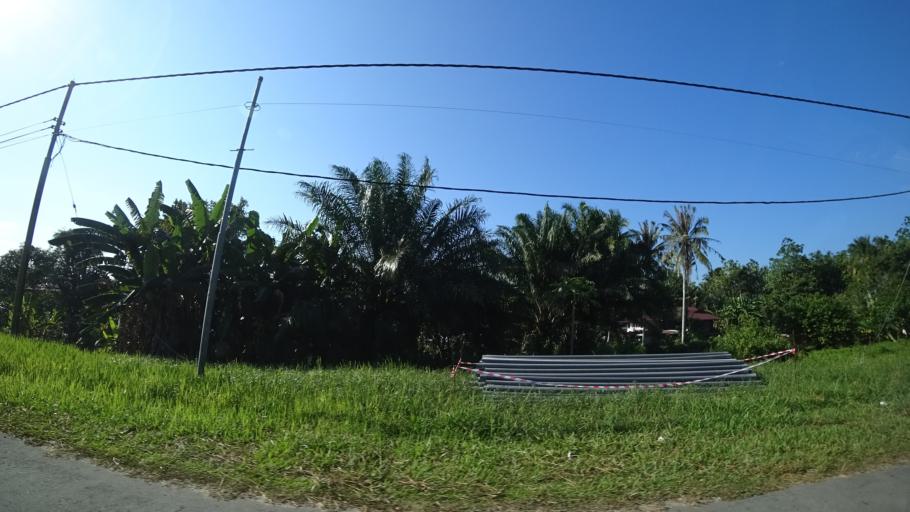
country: BN
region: Tutong
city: Tutong
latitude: 4.6854
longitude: 114.5059
